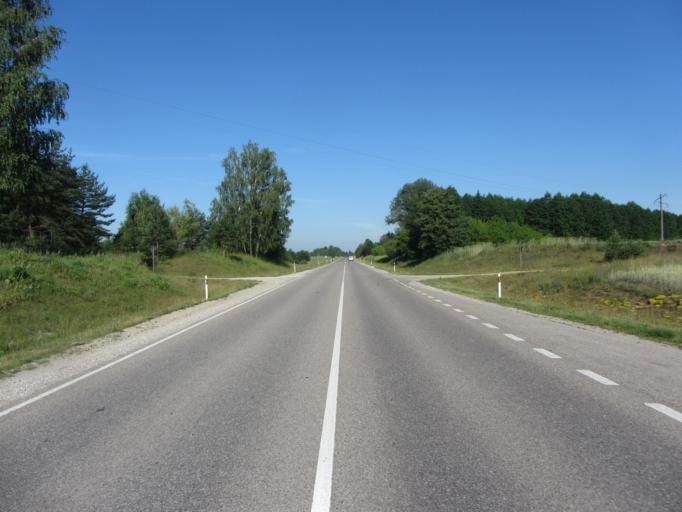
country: LT
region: Alytaus apskritis
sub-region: Alytaus rajonas
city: Daugai
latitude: 54.3663
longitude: 24.3910
